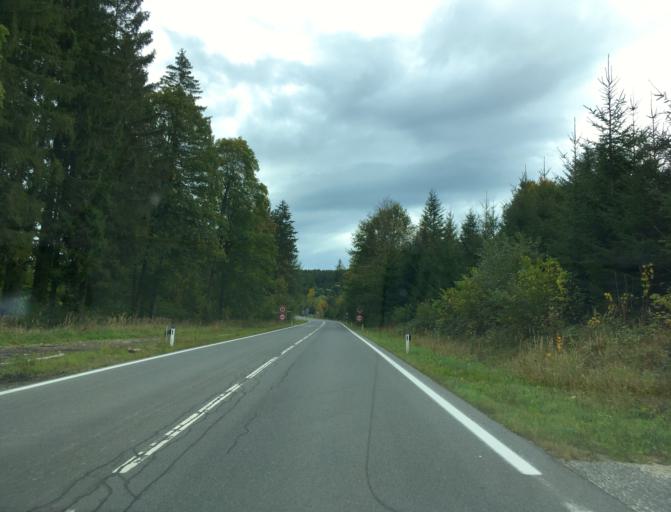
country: AT
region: Lower Austria
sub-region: Politischer Bezirk Neunkirchen
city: Thomasberg
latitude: 47.5495
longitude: 16.1436
